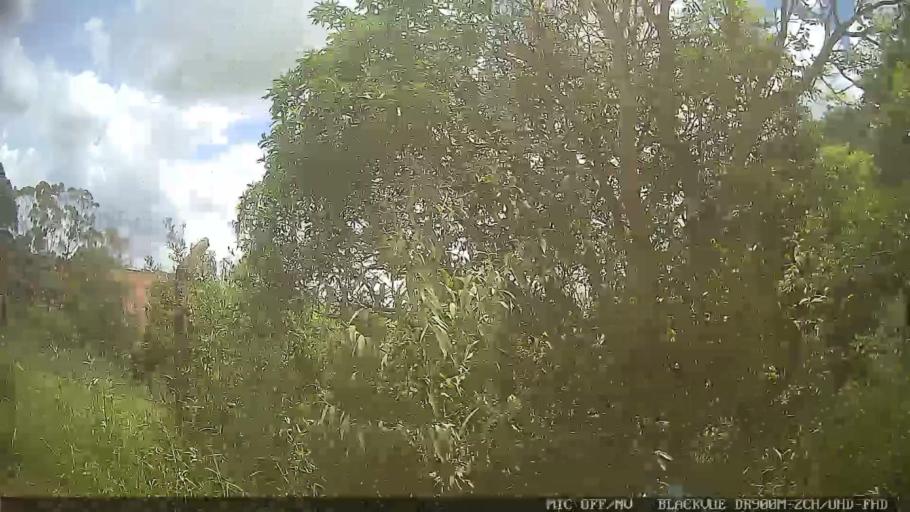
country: BR
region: Sao Paulo
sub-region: Atibaia
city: Atibaia
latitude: -23.0357
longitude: -46.5413
